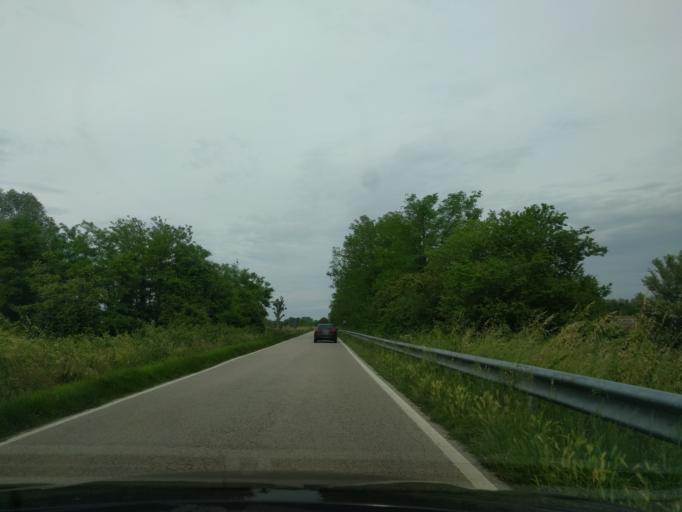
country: IT
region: Veneto
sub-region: Provincia di Rovigo
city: Gavello
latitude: 45.0308
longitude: 11.9368
